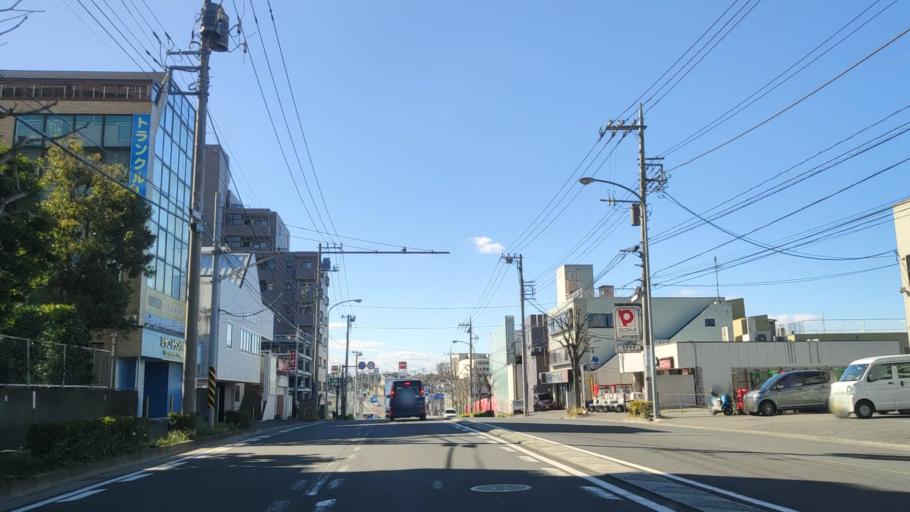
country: JP
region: Kanagawa
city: Minami-rinkan
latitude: 35.4979
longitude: 139.5379
